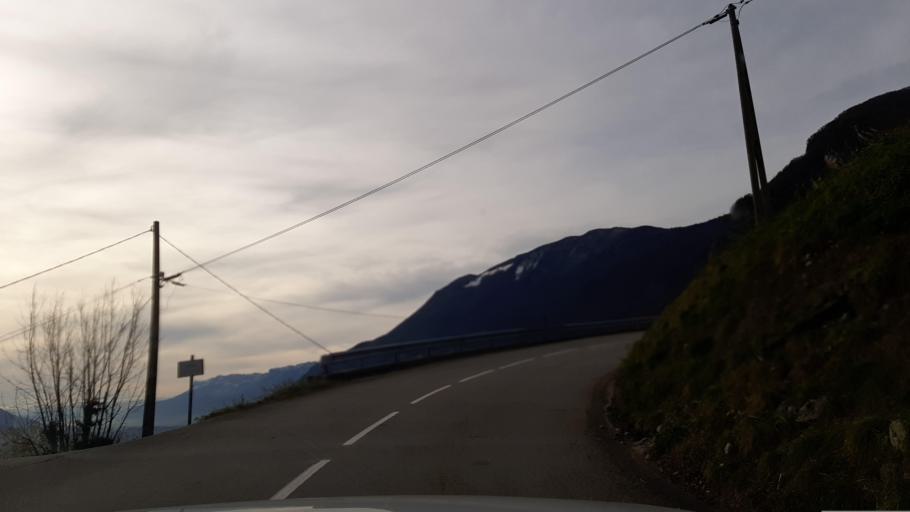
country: FR
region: Rhone-Alpes
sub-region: Departement de la Savoie
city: Coise-Saint-Jean-Pied-Gauthier
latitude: 45.5776
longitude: 6.1503
